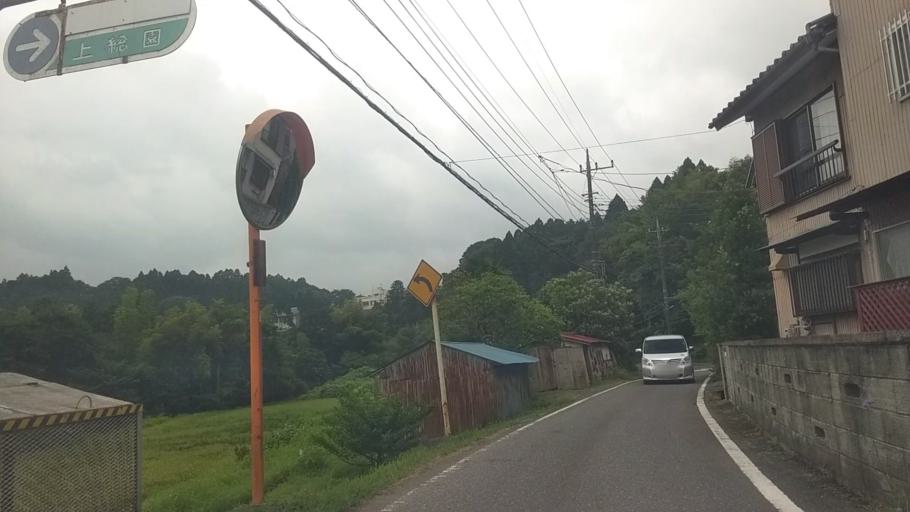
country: JP
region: Chiba
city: Kawaguchi
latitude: 35.2558
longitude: 140.0577
